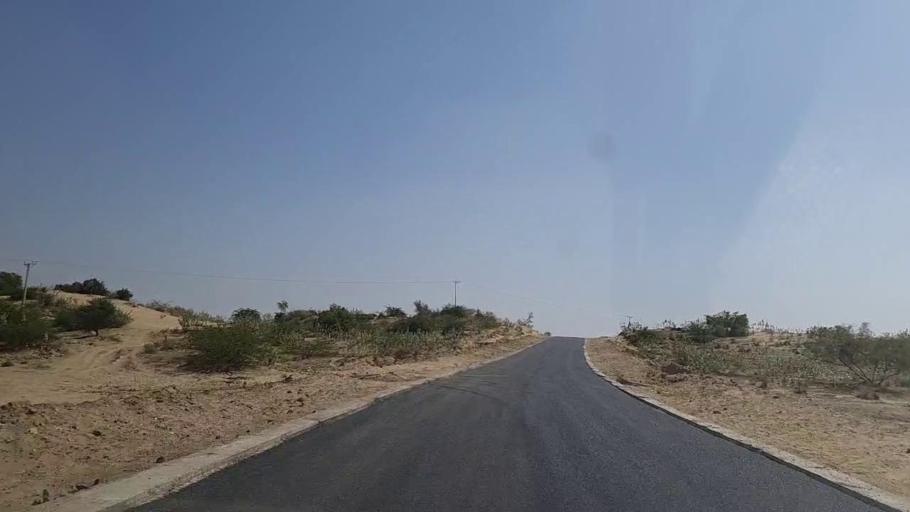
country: PK
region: Sindh
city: Diplo
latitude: 24.4801
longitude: 69.5278
